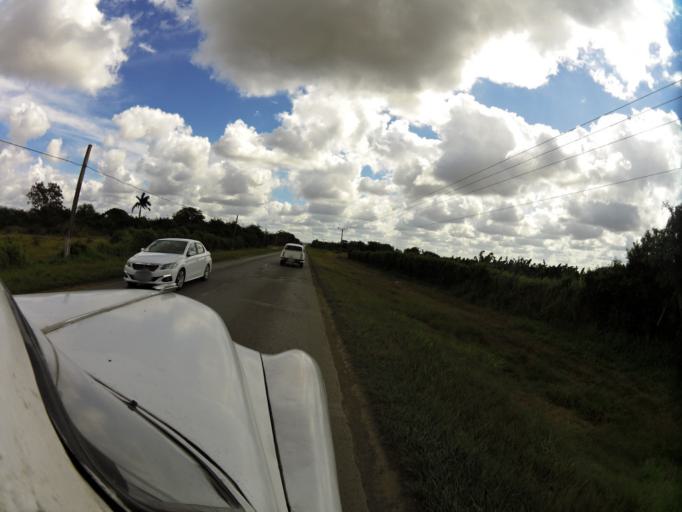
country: CU
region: Las Tunas
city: Las Tunas
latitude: 20.9065
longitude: -76.7725
